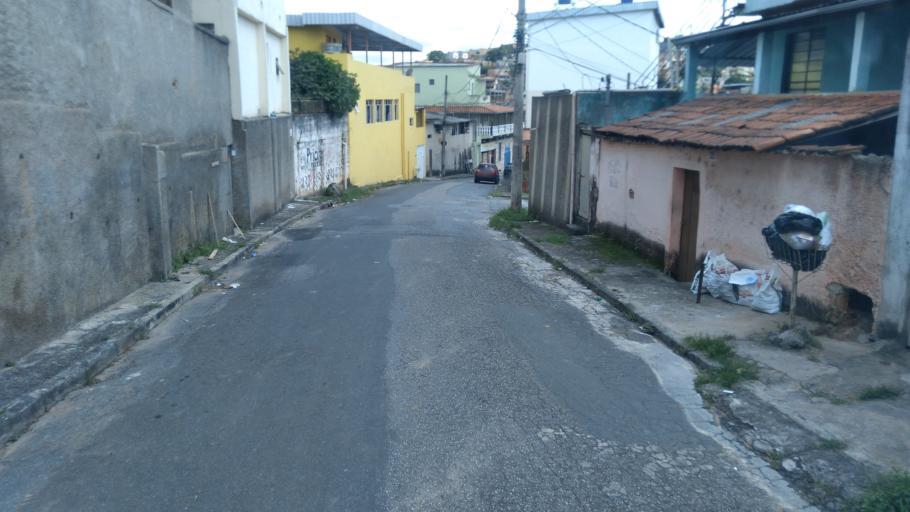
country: BR
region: Minas Gerais
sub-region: Belo Horizonte
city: Belo Horizonte
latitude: -19.8518
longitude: -43.9000
